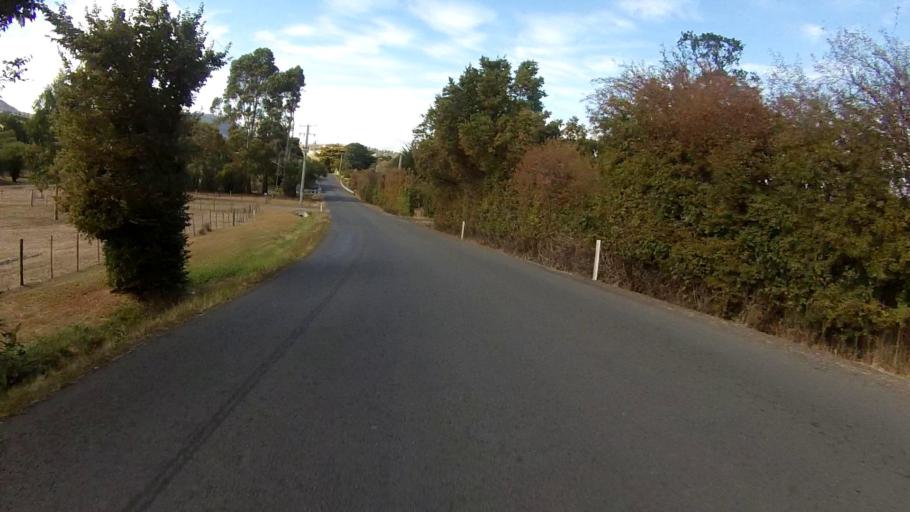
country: AU
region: Tasmania
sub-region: Brighton
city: Old Beach
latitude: -42.7528
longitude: 147.2790
